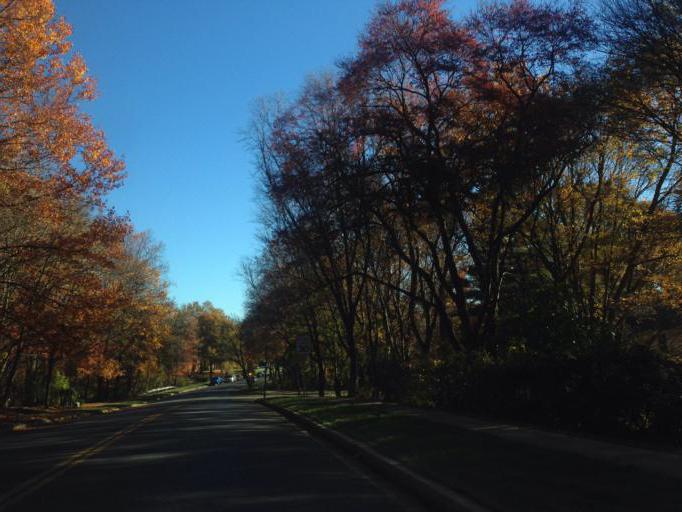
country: US
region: Maryland
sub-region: Howard County
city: Riverside
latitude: 39.1929
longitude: -76.8753
